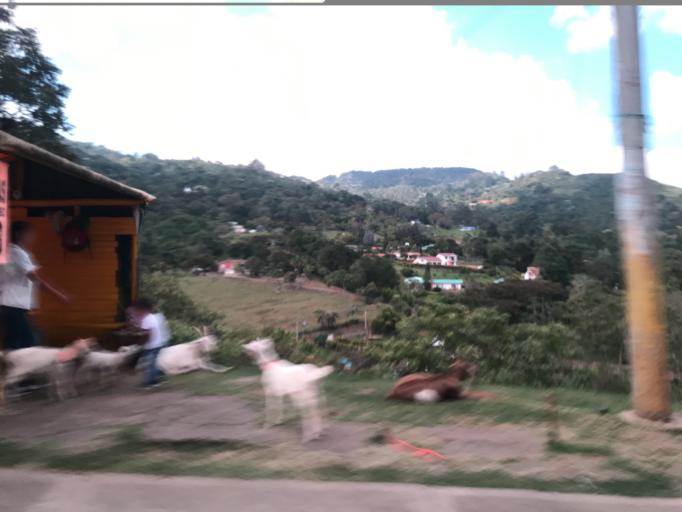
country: CO
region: Valle del Cauca
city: Cali
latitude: 3.4882
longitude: -76.6037
